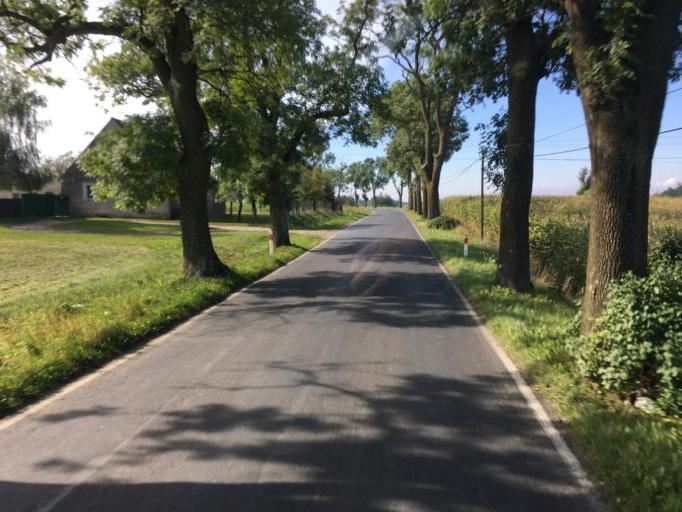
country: PL
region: Kujawsko-Pomorskie
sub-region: Powiat swiecki
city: Lniano
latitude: 53.5173
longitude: 18.1858
